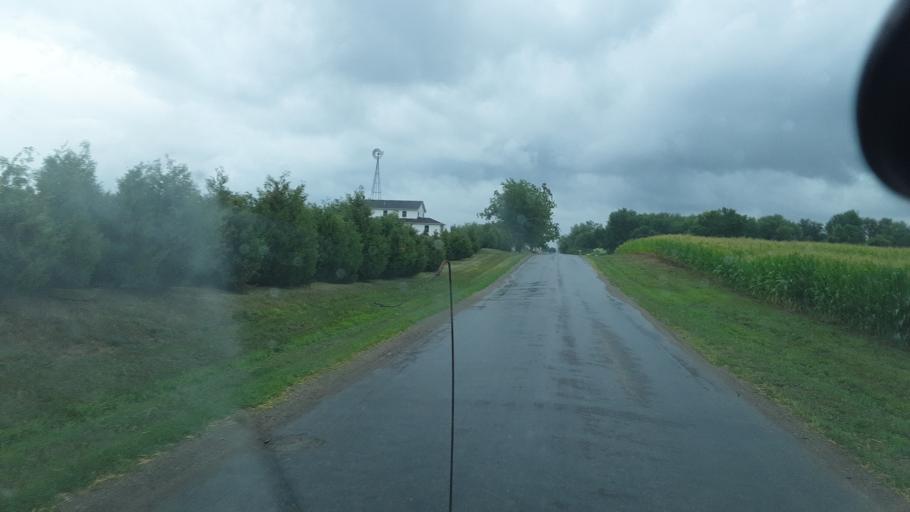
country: US
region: Indiana
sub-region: Steuben County
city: Hamilton
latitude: 41.5708
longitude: -84.7977
